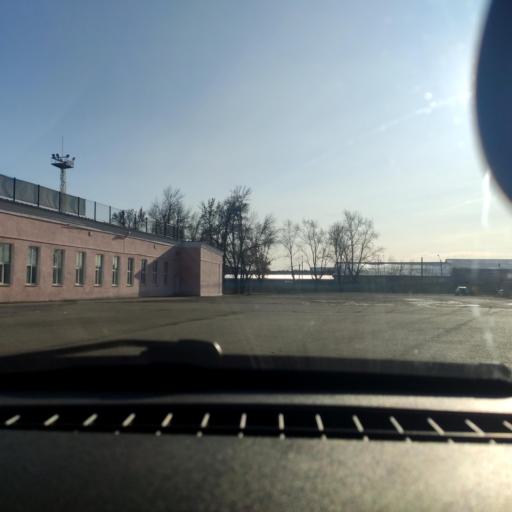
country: RU
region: Bashkortostan
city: Ufa
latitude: 54.7987
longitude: 56.1346
